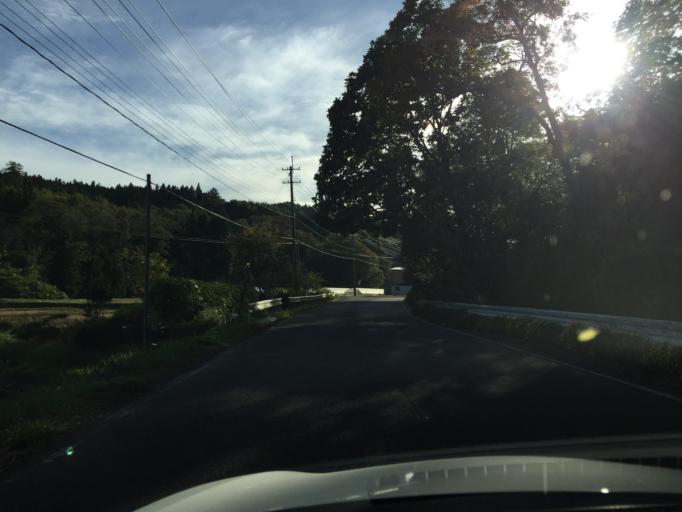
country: JP
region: Fukushima
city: Ishikawa
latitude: 37.2285
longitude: 140.6068
